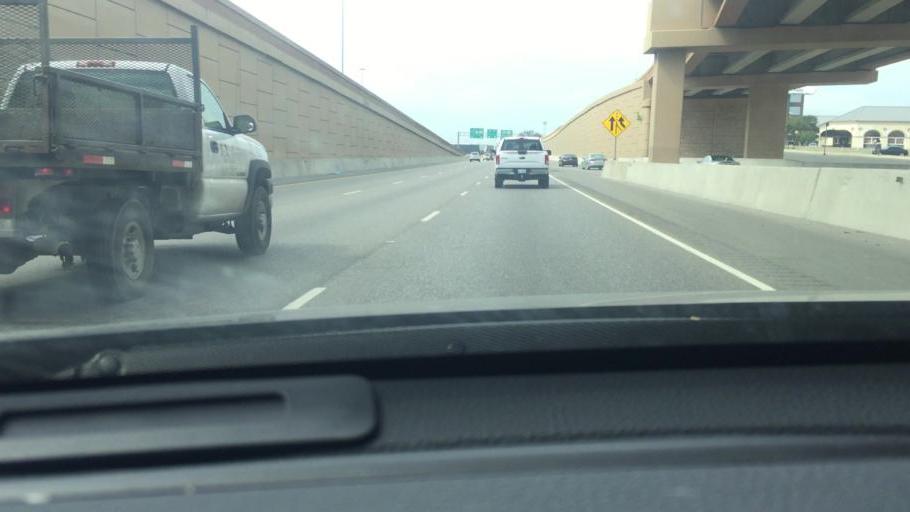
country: US
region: Texas
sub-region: Tarrant County
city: Hurst
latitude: 32.8389
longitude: -97.1899
